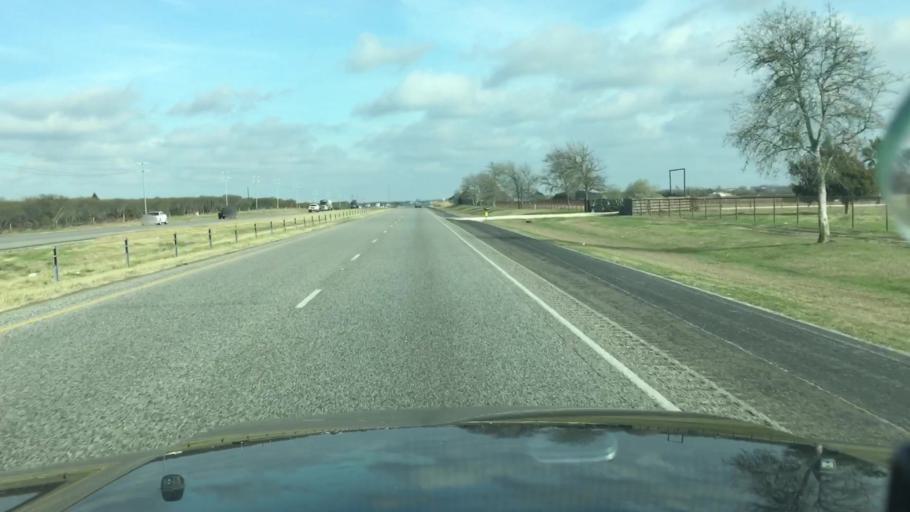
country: US
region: Texas
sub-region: Washington County
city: Brenham
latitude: 30.1376
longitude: -96.3247
